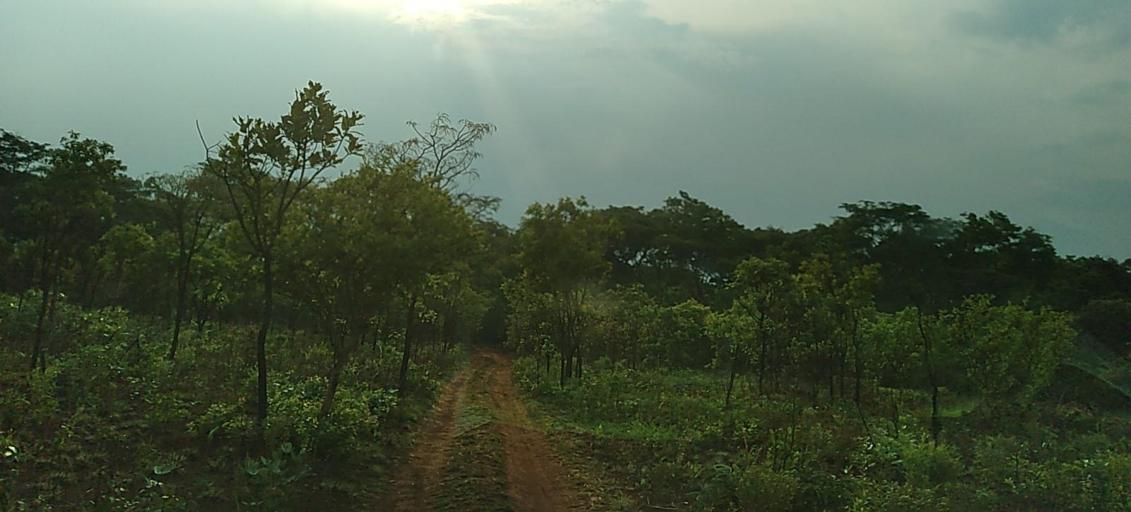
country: ZM
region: North-Western
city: Solwezi
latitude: -12.0416
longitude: 26.0417
